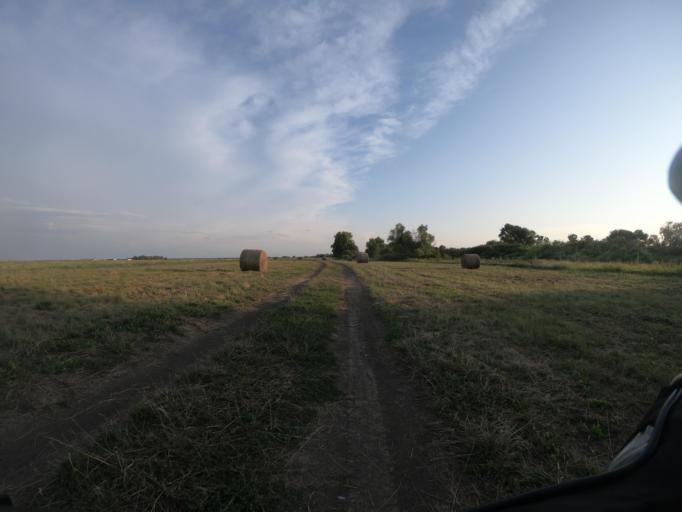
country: HU
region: Borsod-Abauj-Zemplen
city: Mezokeresztes
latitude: 47.7501
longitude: 20.7932
